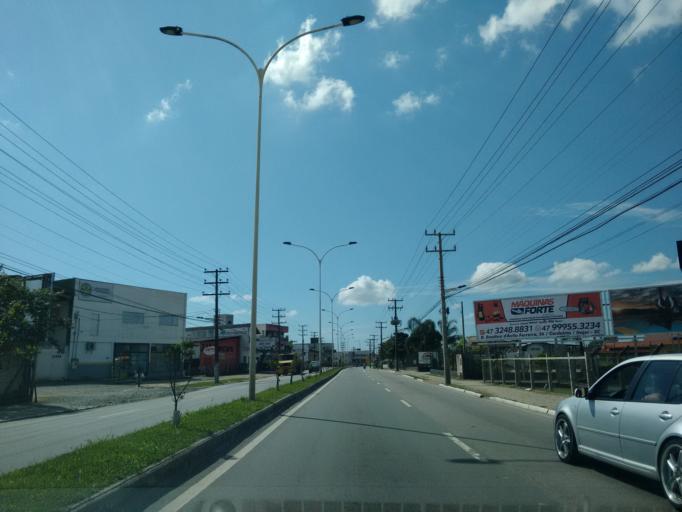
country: BR
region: Santa Catarina
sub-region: Itajai
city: Itajai
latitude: -26.8884
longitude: -48.7066
